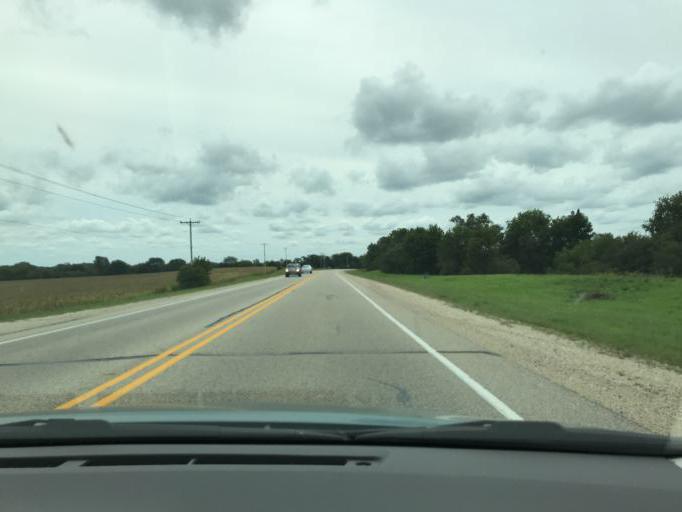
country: US
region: Wisconsin
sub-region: Racine County
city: Bohners Lake
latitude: 42.6441
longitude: -88.2521
